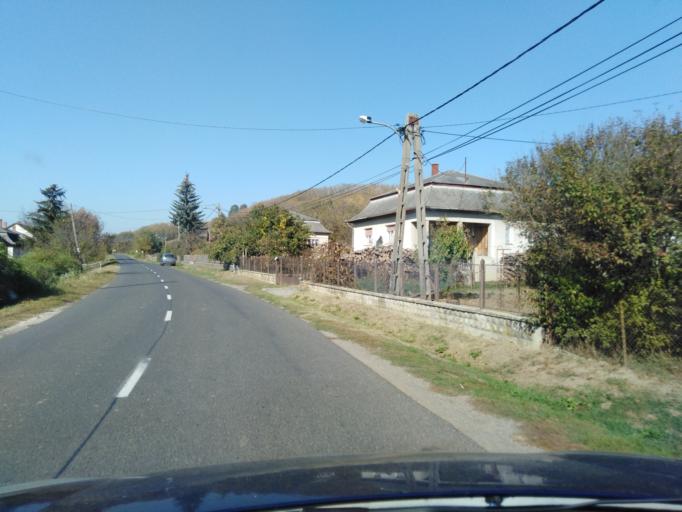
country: HU
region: Nograd
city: Karancskeszi
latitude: 48.1703
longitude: 19.6917
